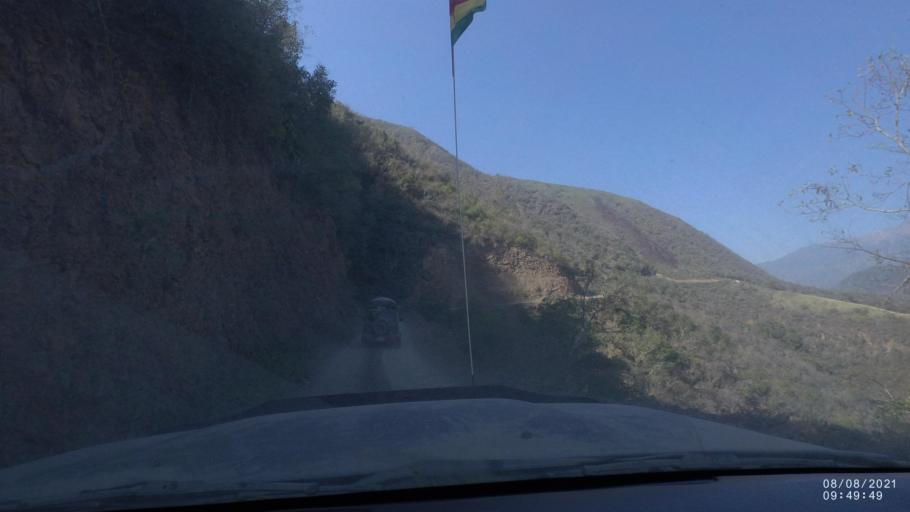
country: BO
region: La Paz
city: Quime
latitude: -16.6186
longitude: -66.7285
